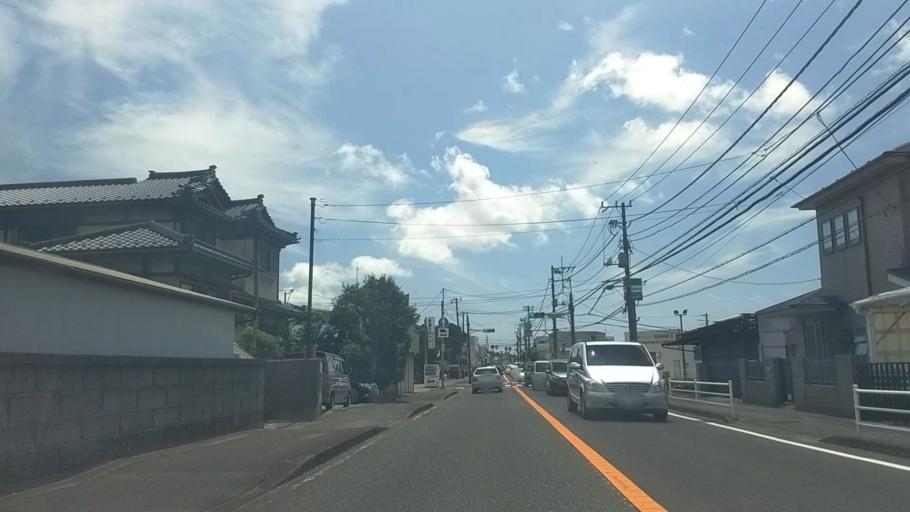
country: JP
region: Kanagawa
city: Yokosuka
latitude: 35.2229
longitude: 139.6437
